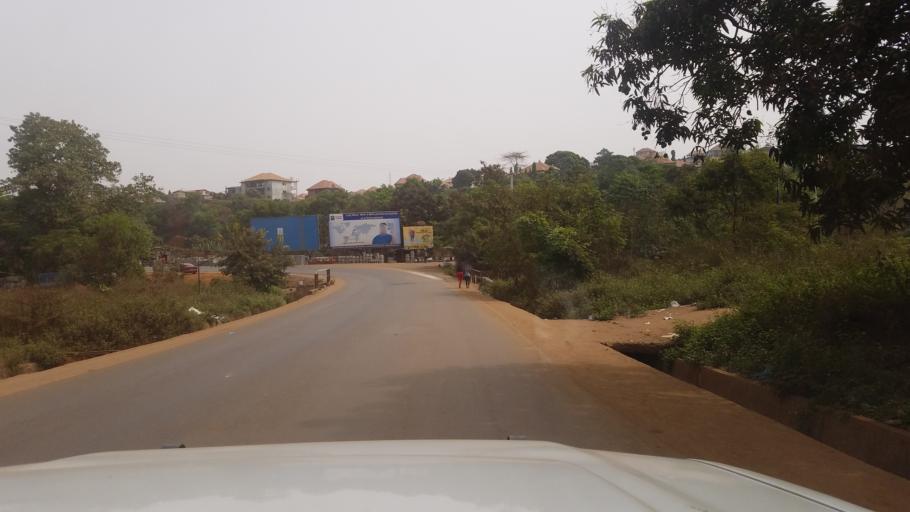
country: GN
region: Conakry
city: Conakry
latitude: 9.6471
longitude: -13.6032
